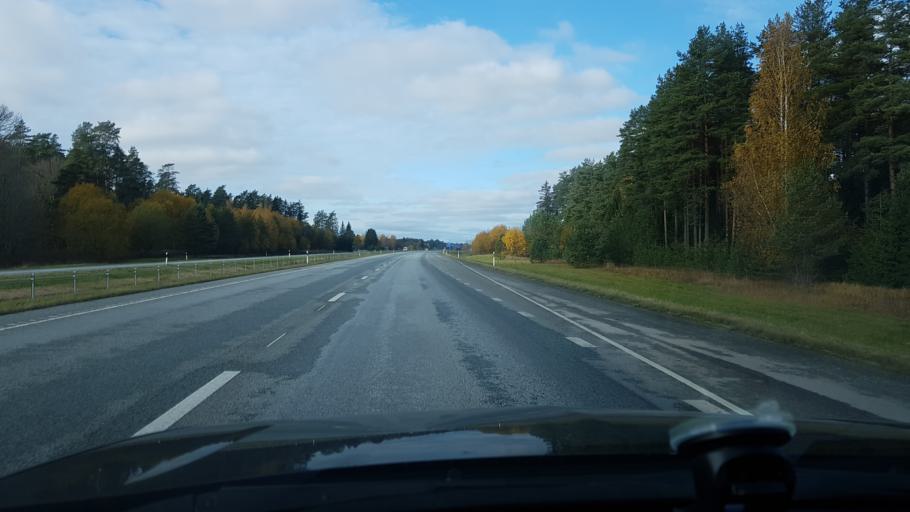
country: EE
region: Laeaene-Virumaa
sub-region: Kadrina vald
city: Kadrina
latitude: 59.4474
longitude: 26.0798
